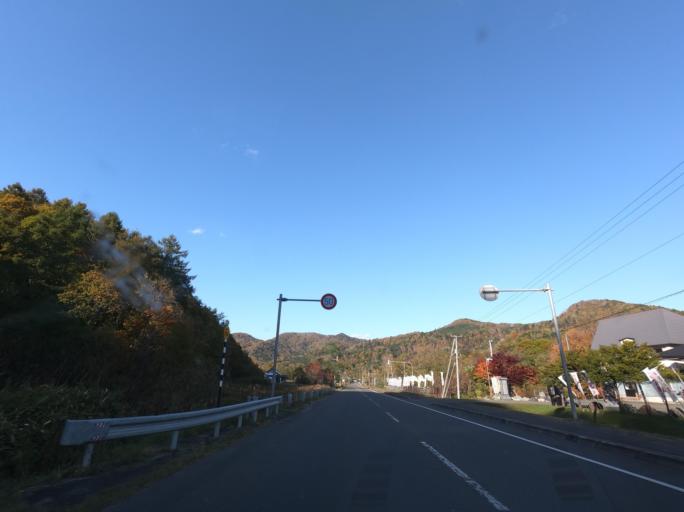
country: JP
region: Hokkaido
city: Iwamizawa
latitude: 43.0014
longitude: 142.0044
